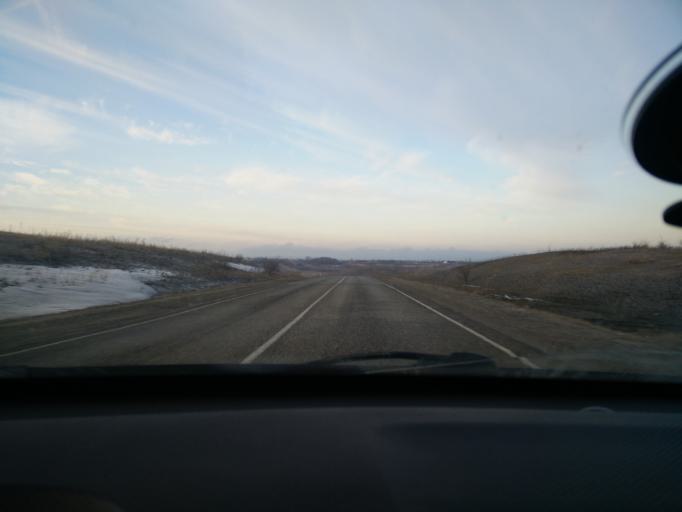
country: RU
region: Stavropol'skiy
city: Balakhonovskoye
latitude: 44.9903
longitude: 41.7085
